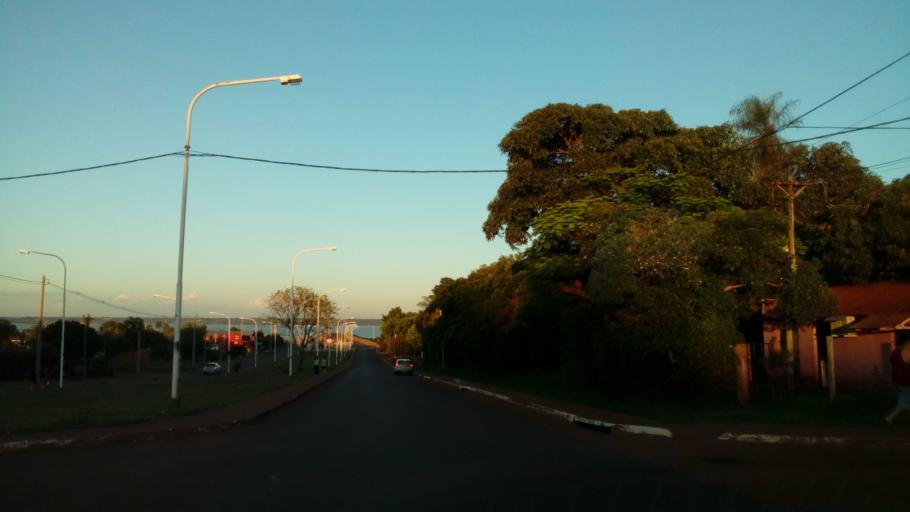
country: AR
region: Misiones
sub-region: Departamento de Capital
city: Posadas
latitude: -27.4273
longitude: -55.8783
